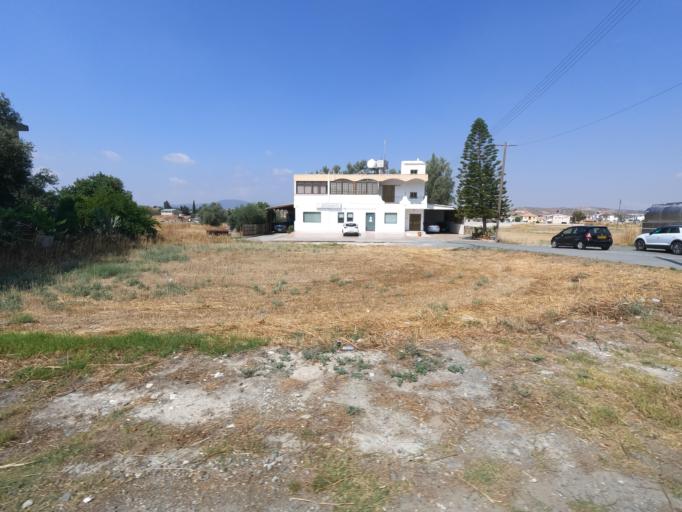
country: CY
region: Lefkosia
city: Lympia
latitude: 34.9987
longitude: 33.4541
